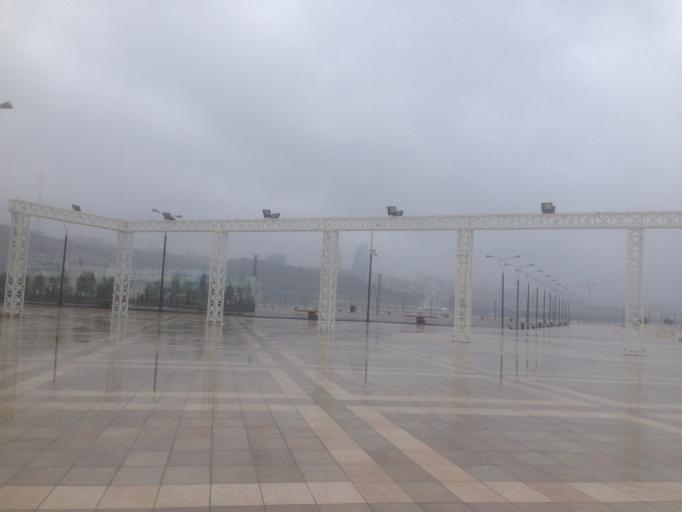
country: AZ
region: Baki
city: Badamdar
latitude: 40.3473
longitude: 49.8462
